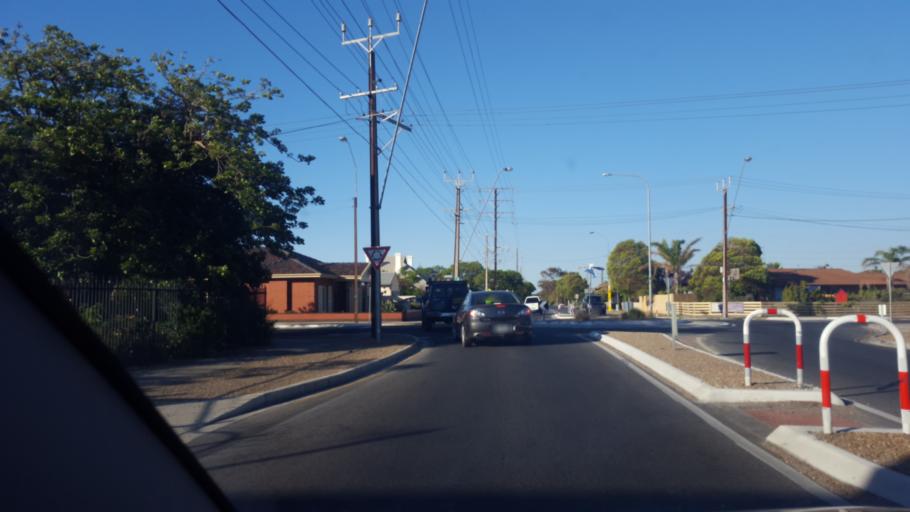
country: AU
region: South Australia
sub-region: Port Adelaide Enfield
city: Birkenhead
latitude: -34.8268
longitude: 138.4894
